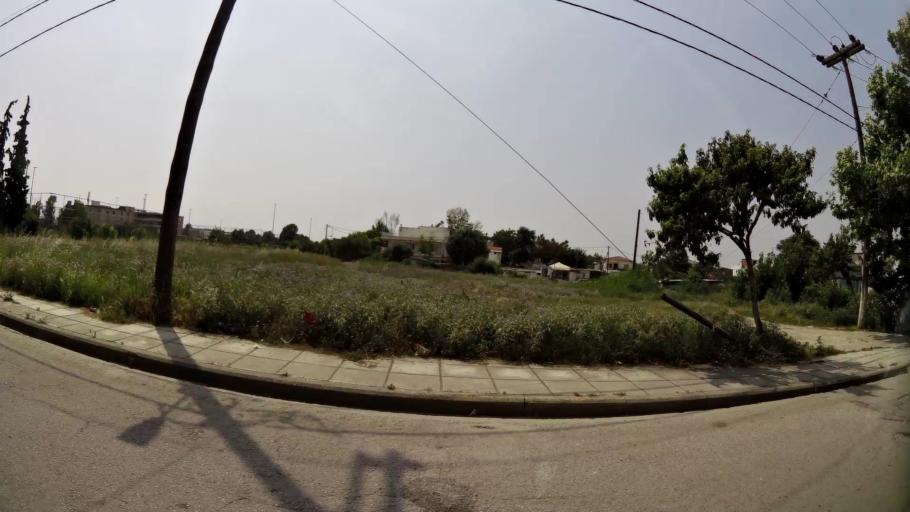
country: GR
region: Central Macedonia
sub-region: Nomos Thessalonikis
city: Menemeni
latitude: 40.6560
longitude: 22.8995
